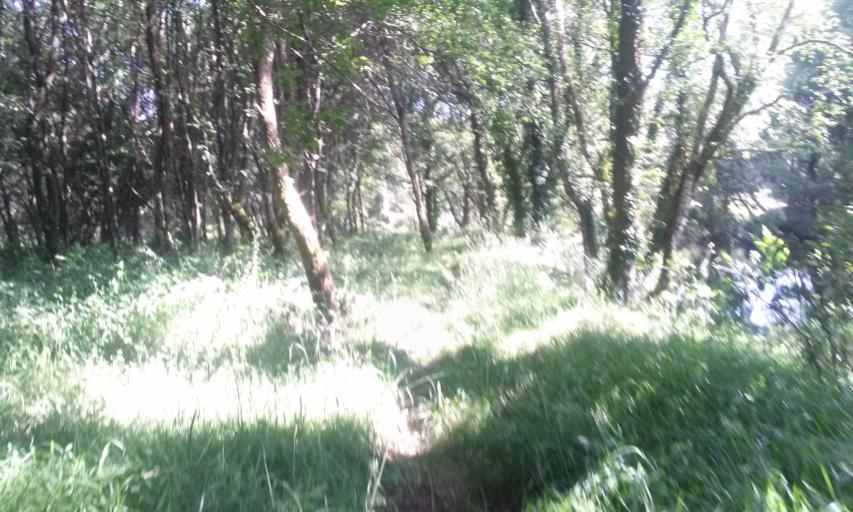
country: ES
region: Galicia
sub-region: Provincia de Lugo
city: Begonte
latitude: 43.1706
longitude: -7.7489
